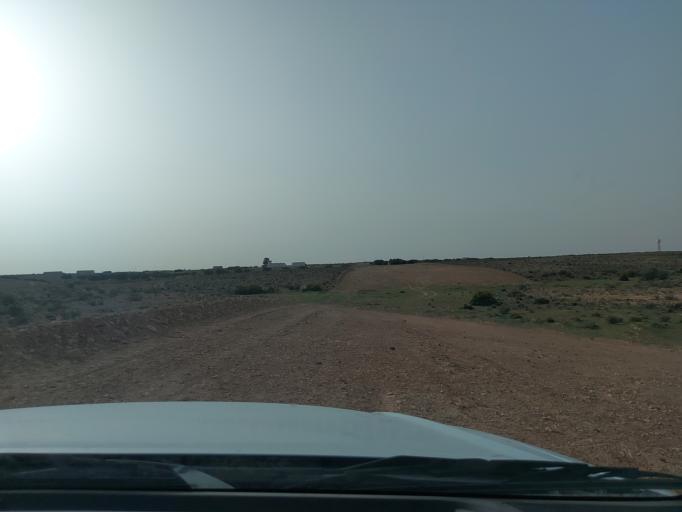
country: TN
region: Madanin
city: Medenine
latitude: 33.3391
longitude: 10.5942
